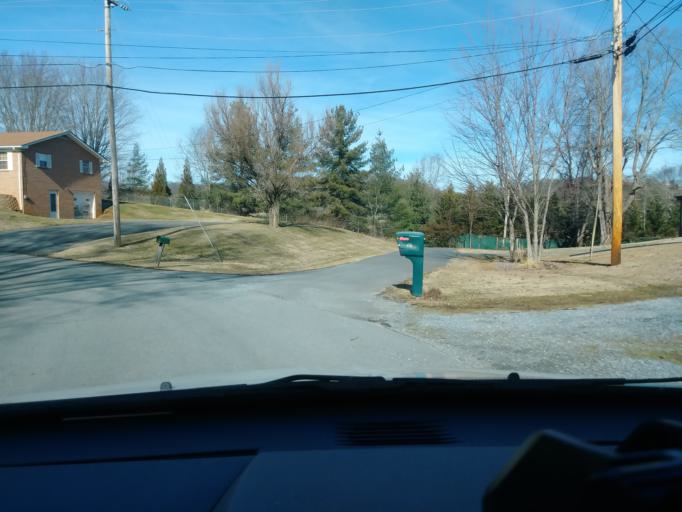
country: US
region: Tennessee
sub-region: Greene County
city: Greeneville
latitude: 36.1280
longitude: -82.8653
